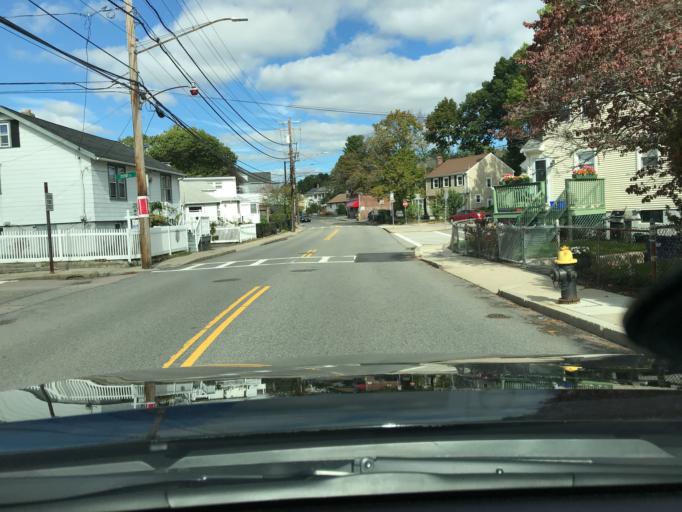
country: US
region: Massachusetts
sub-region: Norfolk County
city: Dedham
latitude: 42.2832
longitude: -71.1694
